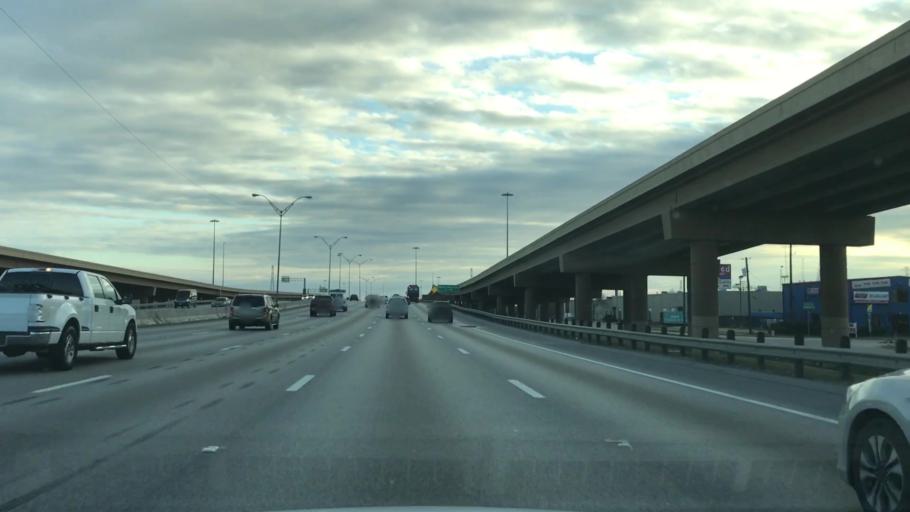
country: US
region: Texas
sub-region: Dallas County
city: Farmers Branch
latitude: 32.8904
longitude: -96.8982
